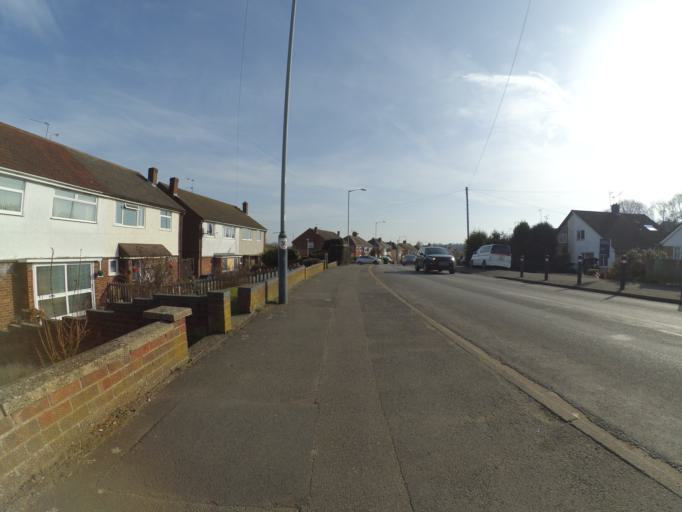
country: GB
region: England
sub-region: Warwickshire
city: Rugby
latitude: 52.3656
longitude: -1.2201
